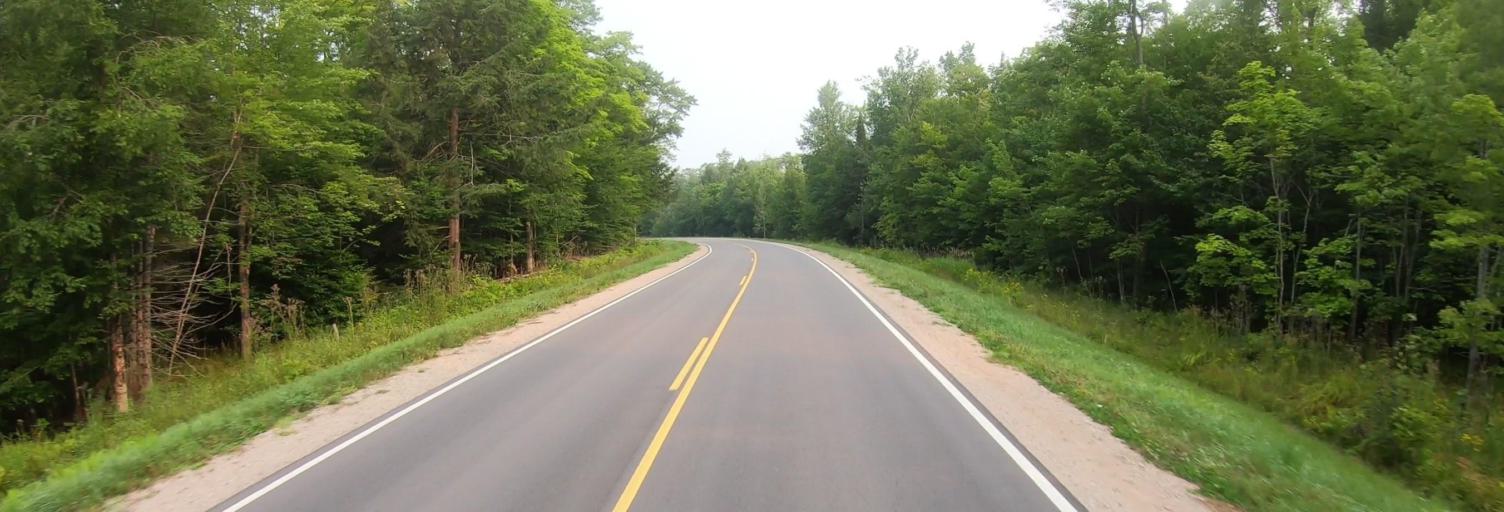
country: US
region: Michigan
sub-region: Luce County
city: Newberry
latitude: 46.4849
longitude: -85.0819
